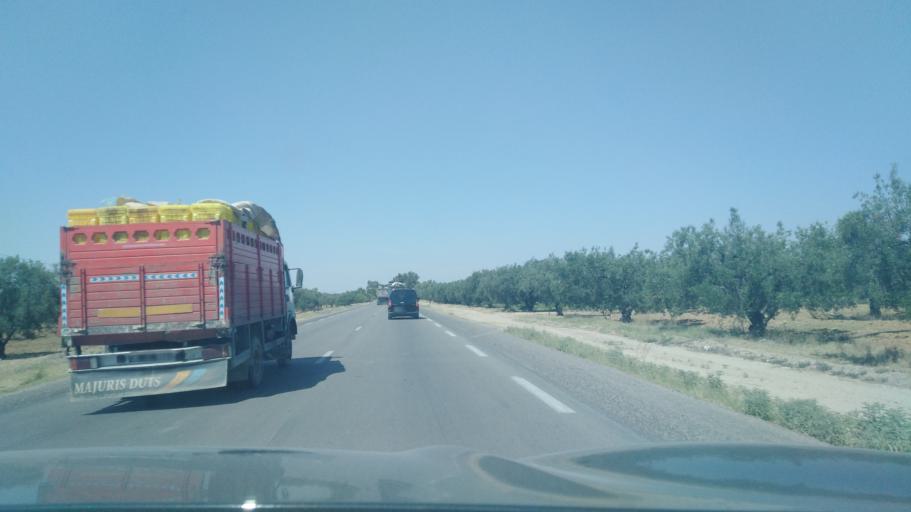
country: TN
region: Al Qayrawan
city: Kairouan
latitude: 35.6105
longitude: 9.9122
